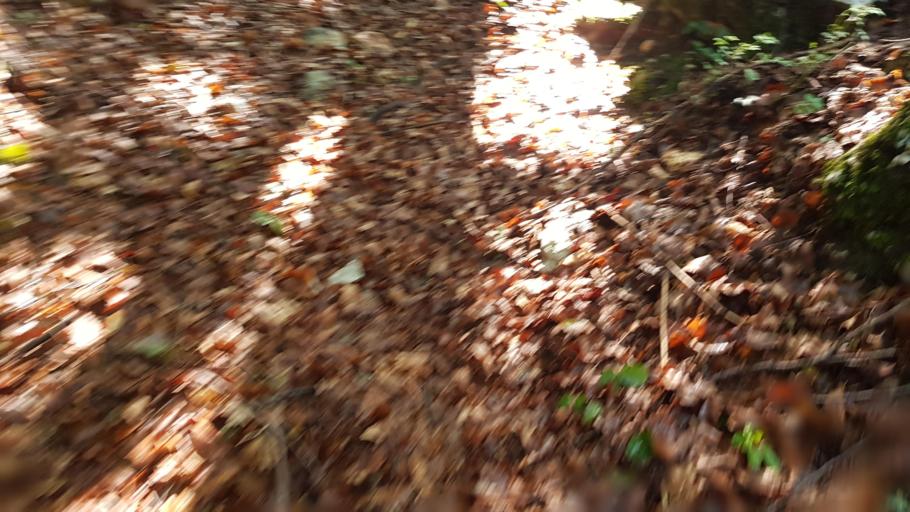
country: IT
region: Trentino-Alto Adige
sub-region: Provincia di Trento
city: Lasino
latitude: 46.0145
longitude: 10.9952
